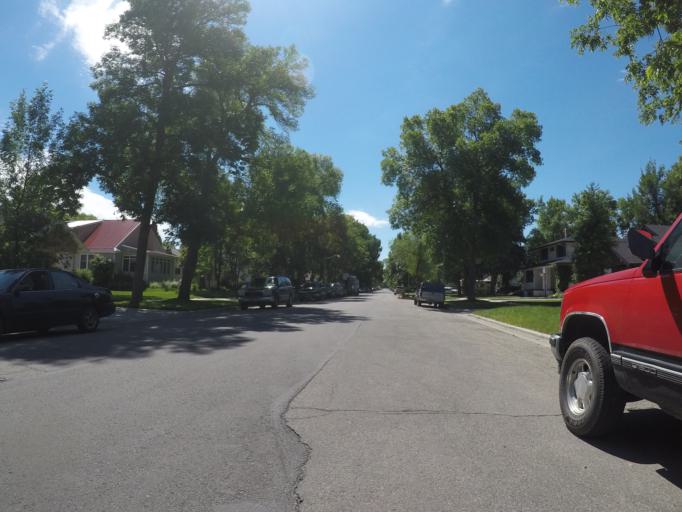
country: US
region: Montana
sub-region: Yellowstone County
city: Billings
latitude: 45.7889
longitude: -108.5197
